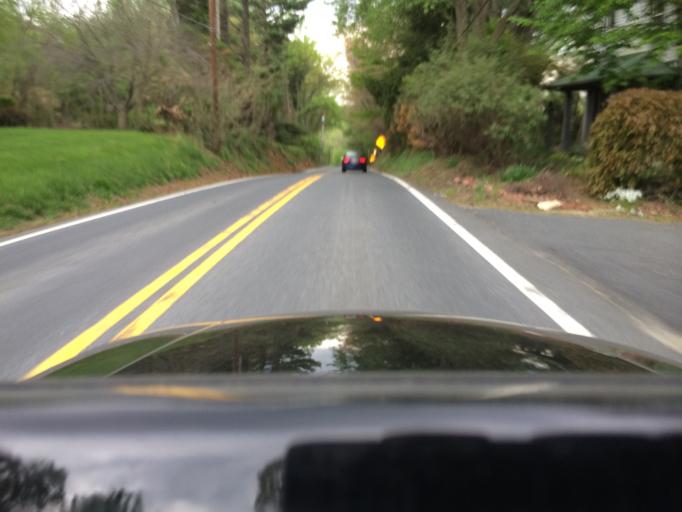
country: US
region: Maryland
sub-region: Carroll County
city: Sykesville
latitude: 39.4091
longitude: -77.0145
